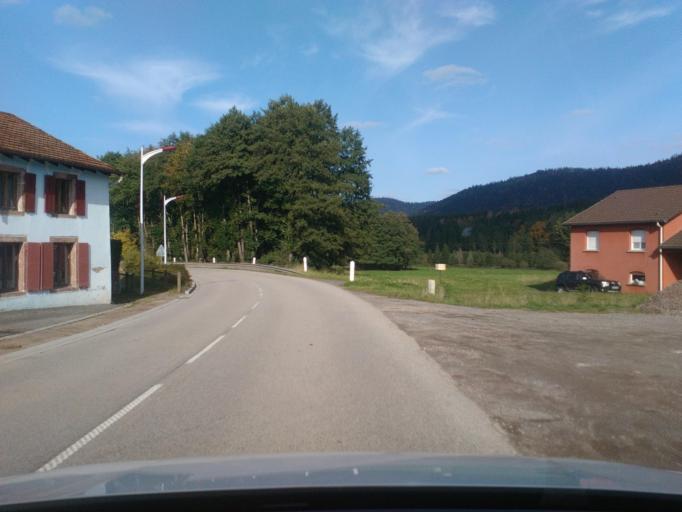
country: FR
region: Lorraine
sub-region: Departement des Vosges
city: Senones
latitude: 48.4097
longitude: 7.0506
